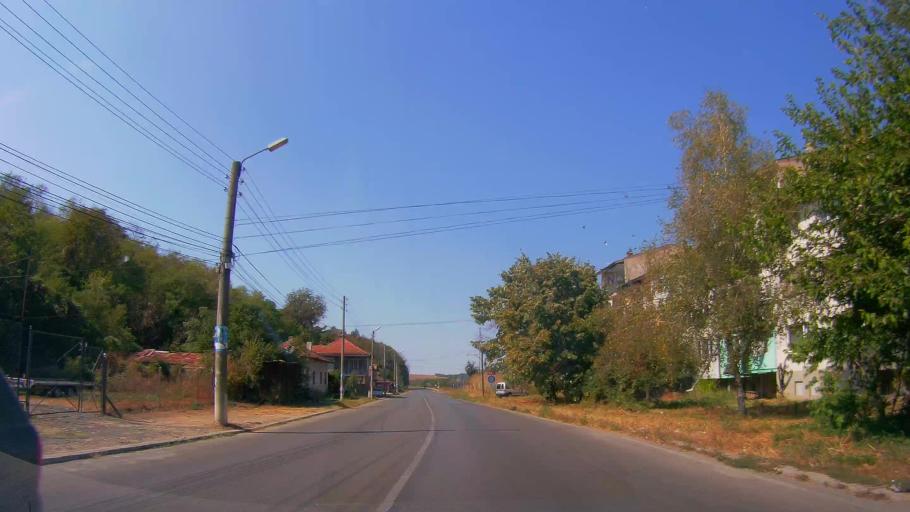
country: BG
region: Razgrad
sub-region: Obshtina Tsar Kaloyan
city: Tsar Kaloyan
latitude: 43.6119
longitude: 26.2311
